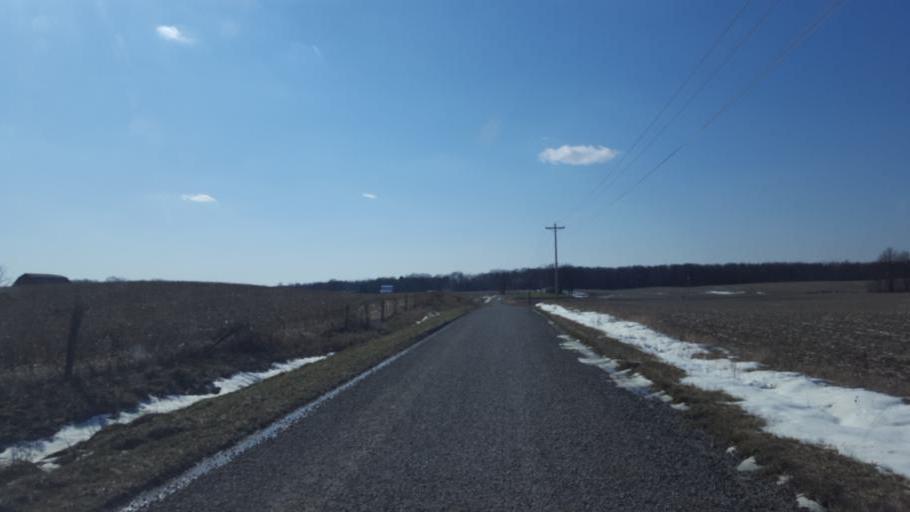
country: US
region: Ohio
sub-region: Morrow County
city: Mount Gilead
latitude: 40.5072
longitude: -82.7743
